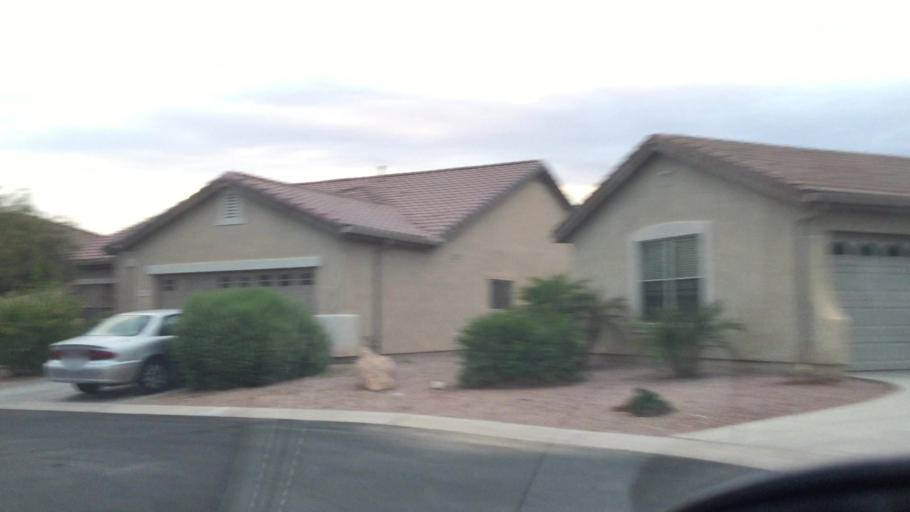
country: US
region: Arizona
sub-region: Maricopa County
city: Gilbert
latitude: 33.3221
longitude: -111.7089
